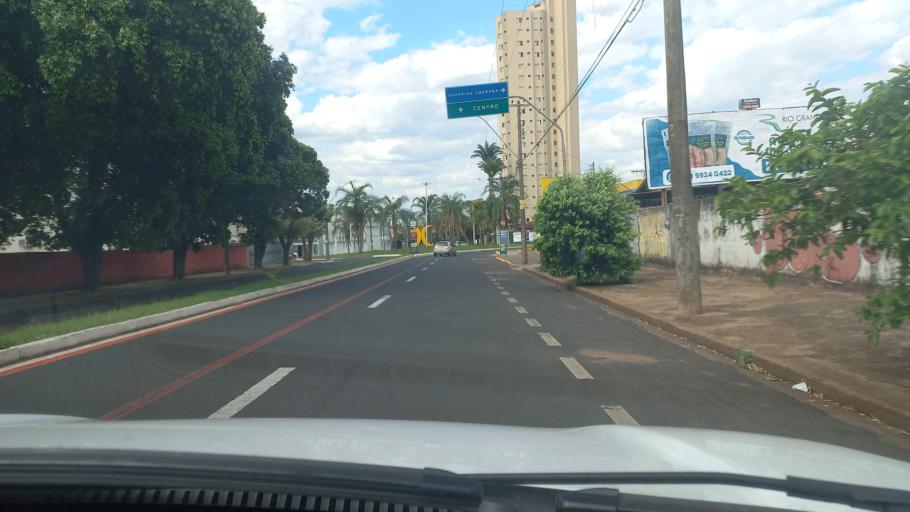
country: BR
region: Minas Gerais
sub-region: Uberaba
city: Uberaba
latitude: -19.7608
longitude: -47.9576
